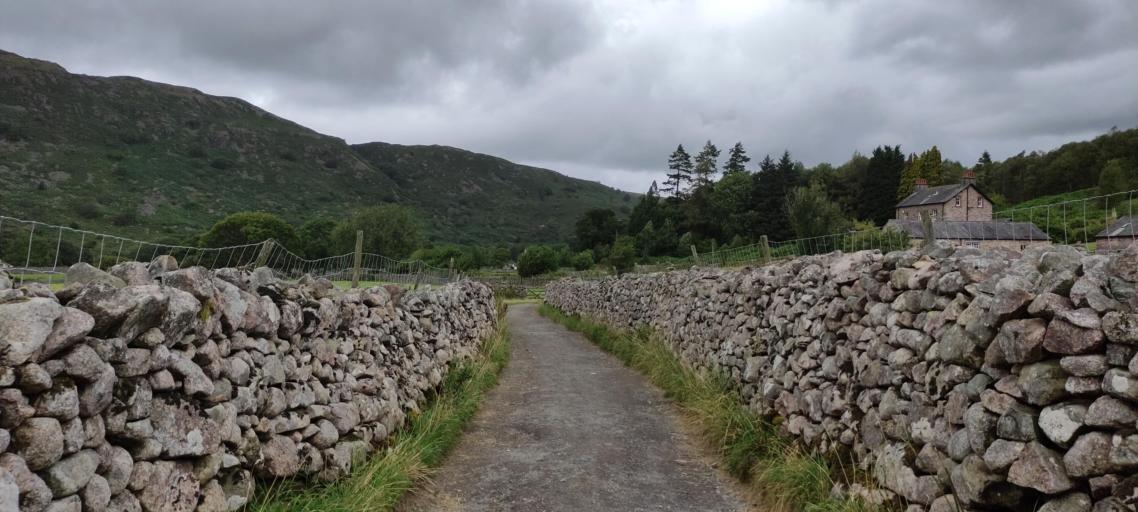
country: GB
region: England
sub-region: Cumbria
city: Millom
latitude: 54.3920
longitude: -3.2708
